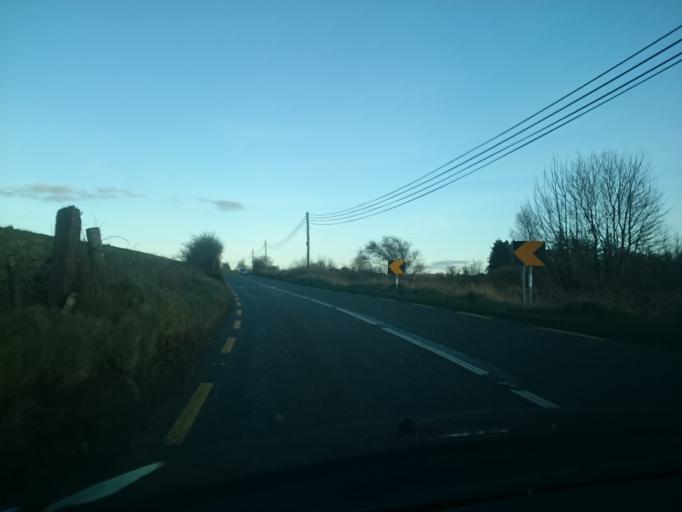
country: IE
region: Connaught
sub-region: Maigh Eo
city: Kiltamagh
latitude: 53.7917
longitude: -9.0922
